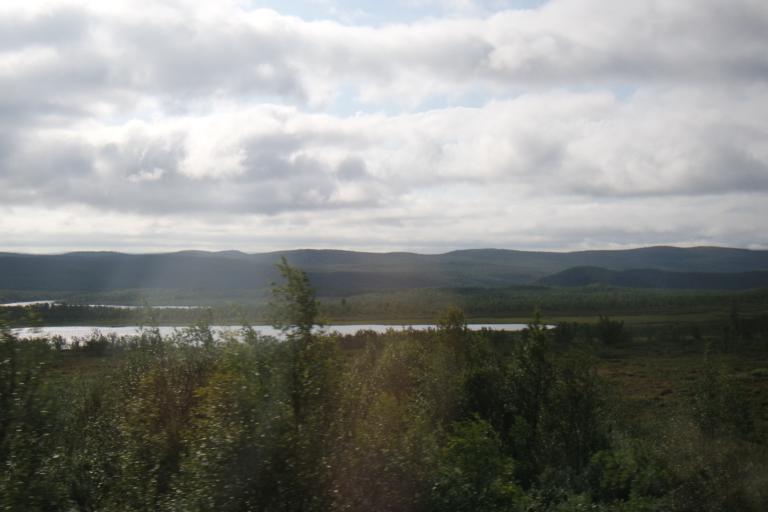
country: NO
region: Finnmark Fylke
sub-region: Karasjok
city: Karasjohka
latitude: 69.7282
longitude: 25.2345
